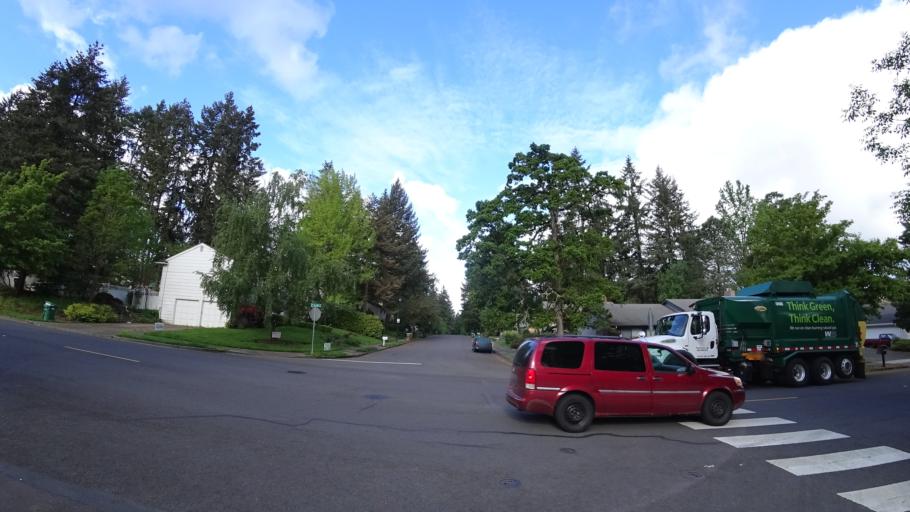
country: US
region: Oregon
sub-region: Washington County
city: Beaverton
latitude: 45.4677
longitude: -122.8197
